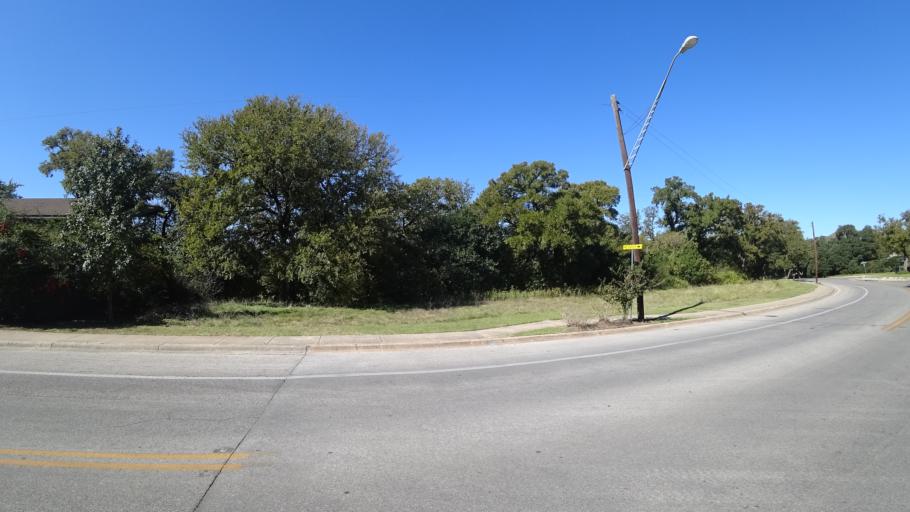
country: US
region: Texas
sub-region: Travis County
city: Austin
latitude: 30.3308
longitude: -97.7460
